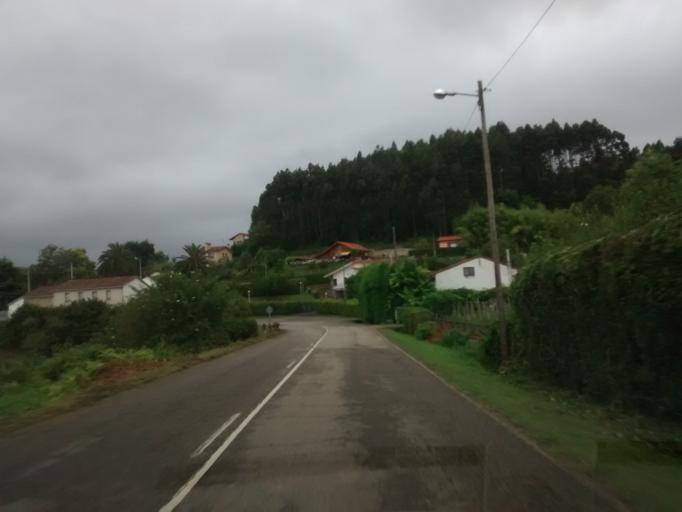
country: ES
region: Asturias
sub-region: Province of Asturias
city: Villaviciosa
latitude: 43.5206
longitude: -5.4006
